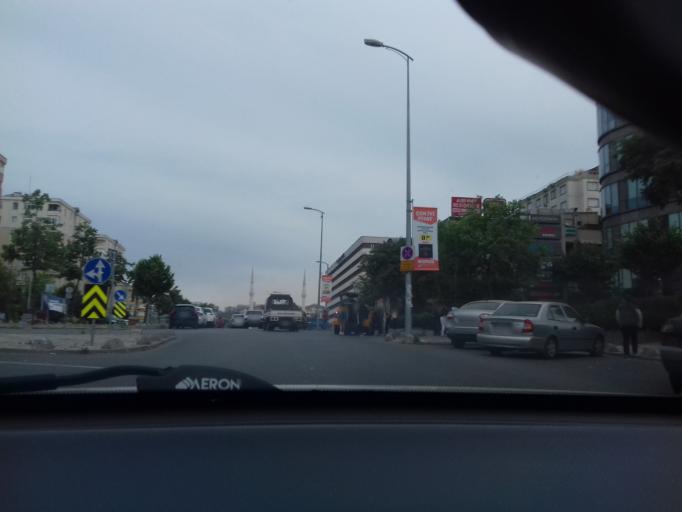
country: TR
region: Istanbul
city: Sultanbeyli
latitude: 40.9291
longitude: 29.3062
